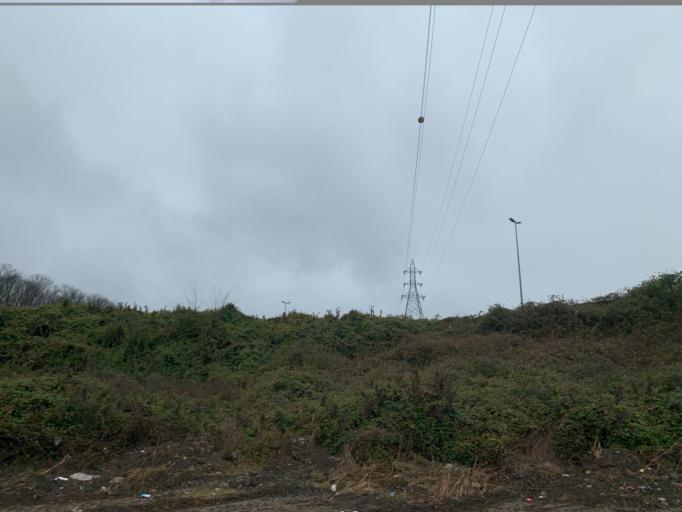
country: IR
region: Mazandaran
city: Amol
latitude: 36.3991
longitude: 52.3468
